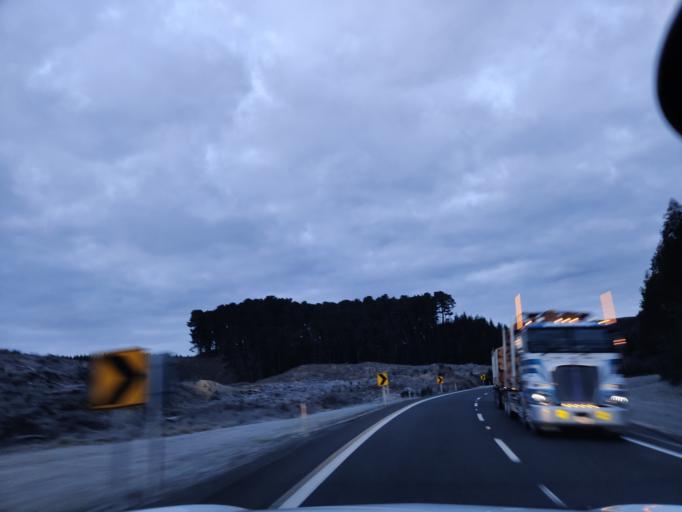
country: NZ
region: Waikato
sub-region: South Waikato District
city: Tokoroa
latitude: -38.4096
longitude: 176.0522
